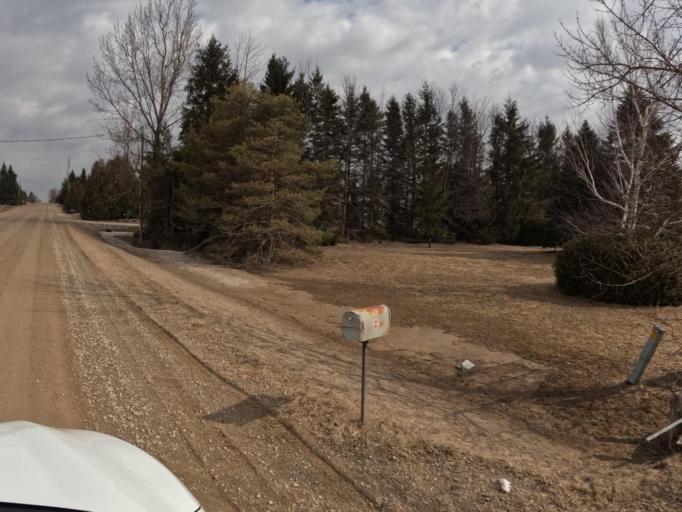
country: CA
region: Ontario
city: Orangeville
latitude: 43.9380
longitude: -80.1896
